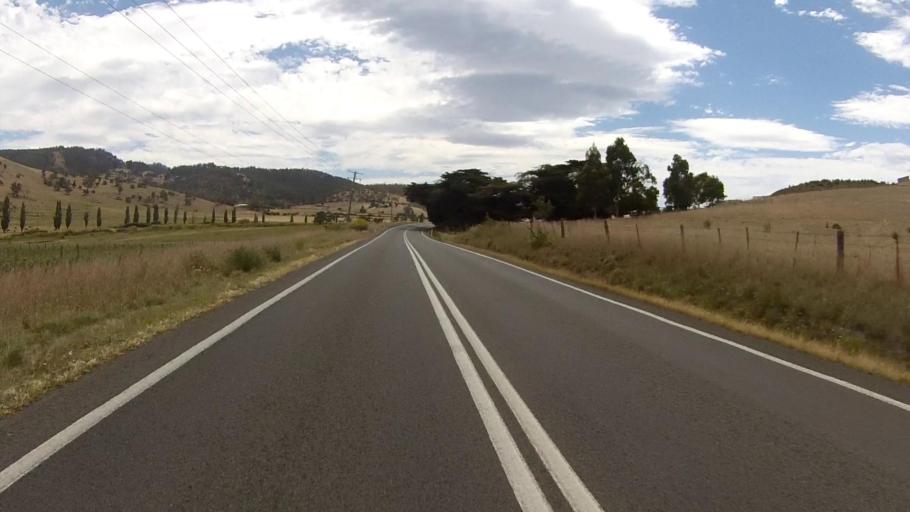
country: AU
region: Tasmania
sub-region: Brighton
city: Old Beach
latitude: -42.6779
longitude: 147.3546
